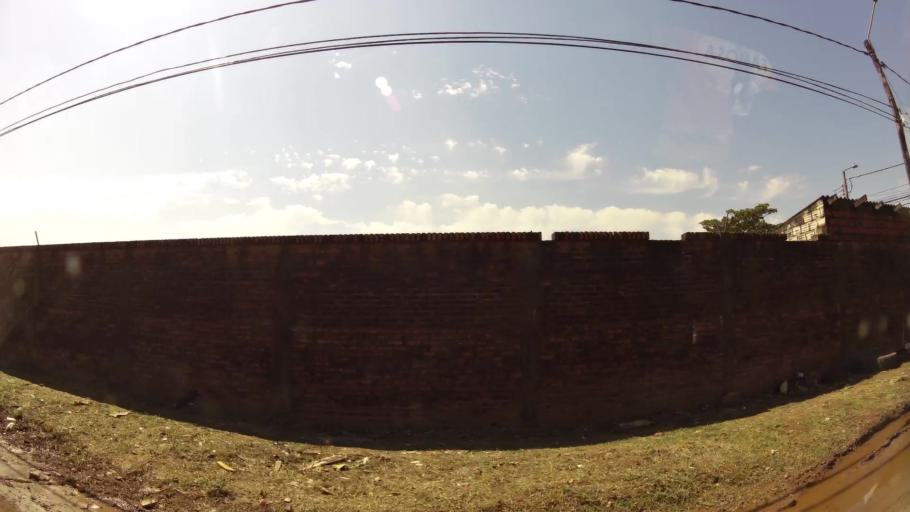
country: BO
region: Santa Cruz
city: Santa Cruz de la Sierra
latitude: -17.7328
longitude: -63.1503
